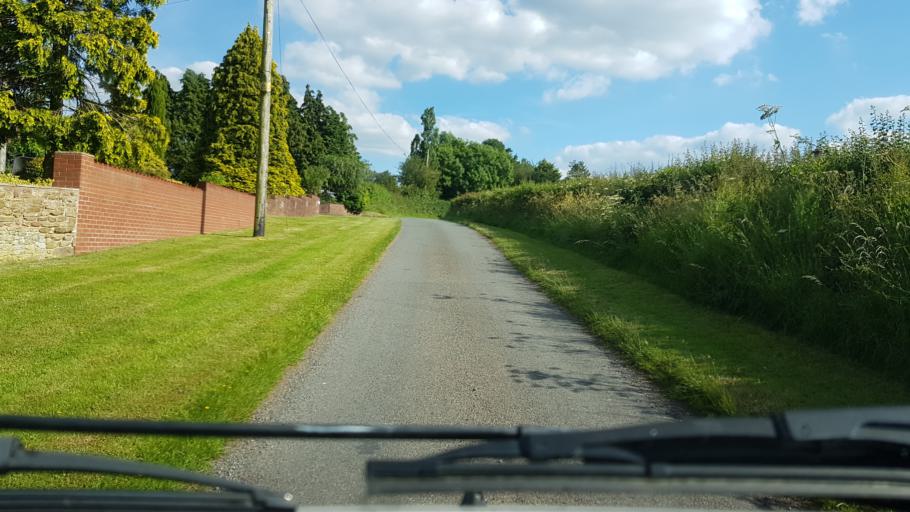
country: GB
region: England
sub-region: Worcestershire
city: Bewdley
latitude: 52.3419
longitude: -2.3305
